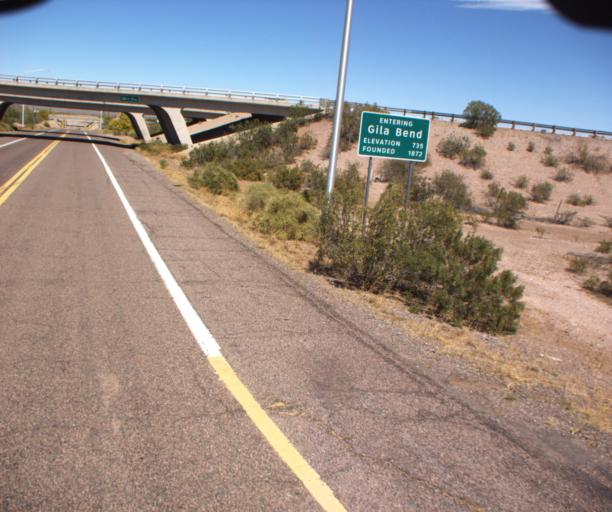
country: US
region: Arizona
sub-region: Maricopa County
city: Gila Bend
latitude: 32.9393
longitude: -112.7339
